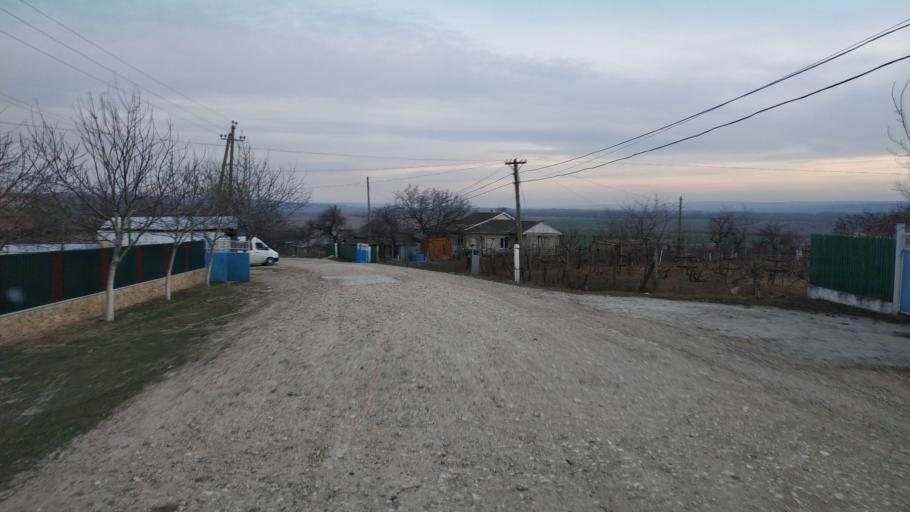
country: MD
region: Hincesti
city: Dancu
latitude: 46.7467
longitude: 28.2091
